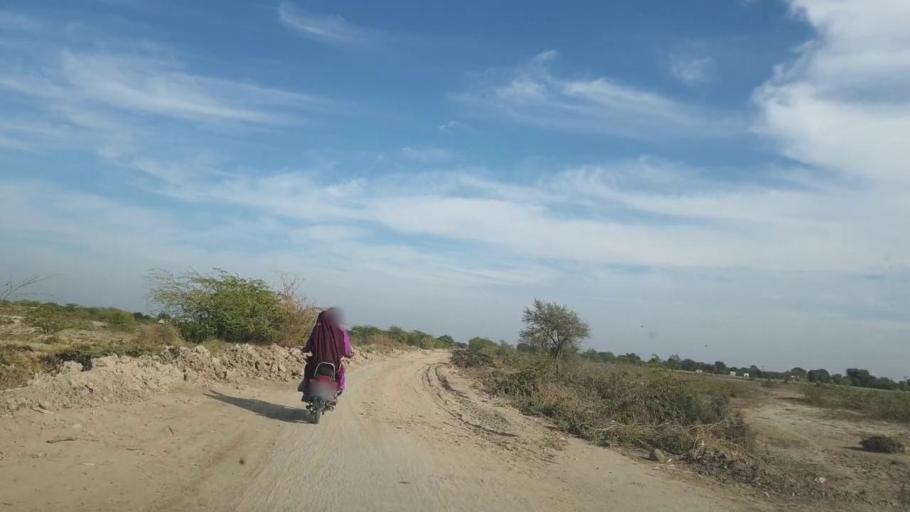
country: PK
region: Sindh
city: Pithoro
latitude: 25.6452
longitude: 69.3633
